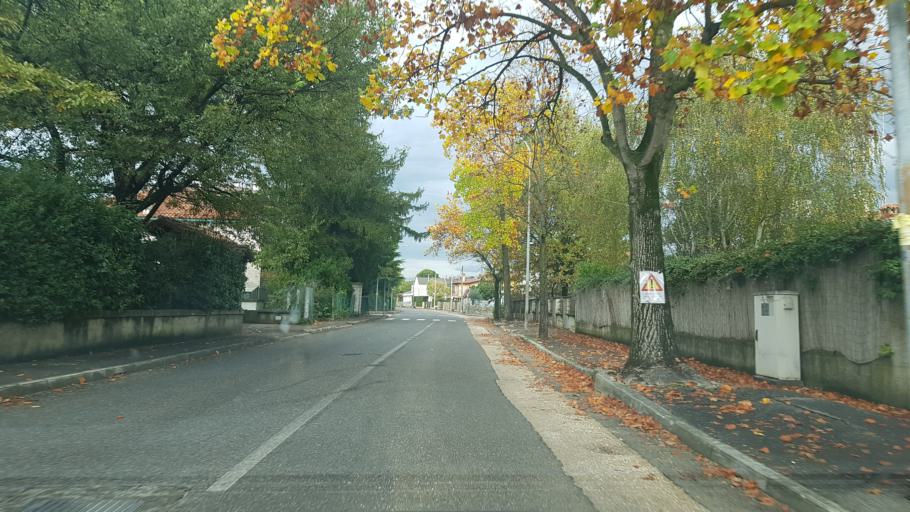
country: IT
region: Friuli Venezia Giulia
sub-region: Provincia di Gorizia
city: Ronchi dei Legionari
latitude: 45.8261
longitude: 13.5120
